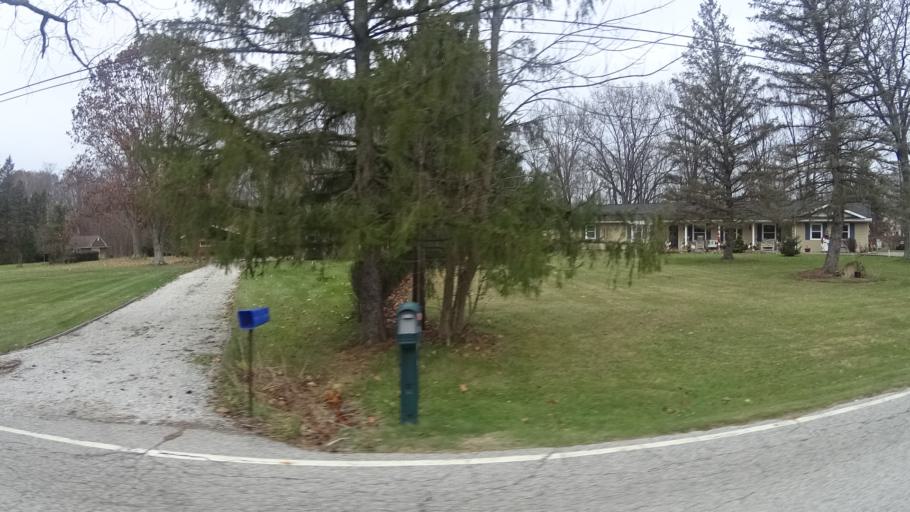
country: US
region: Ohio
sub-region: Cuyahoga County
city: Strongsville
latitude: 41.2895
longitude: -81.9071
